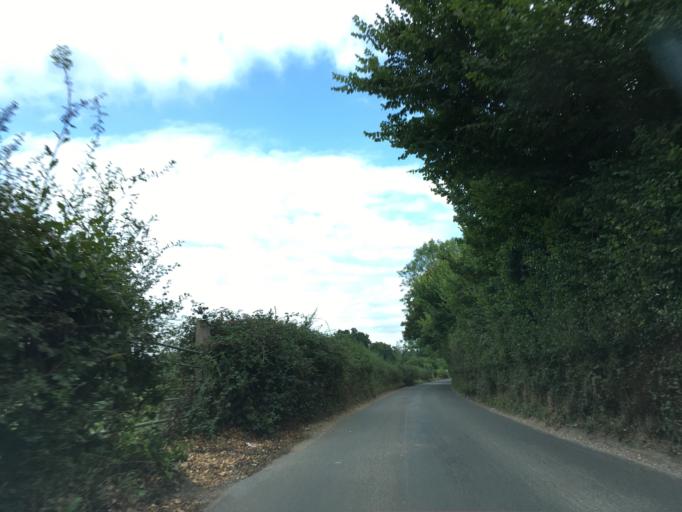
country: GB
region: England
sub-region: Hampshire
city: Colden Common
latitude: 50.9960
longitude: -1.3307
